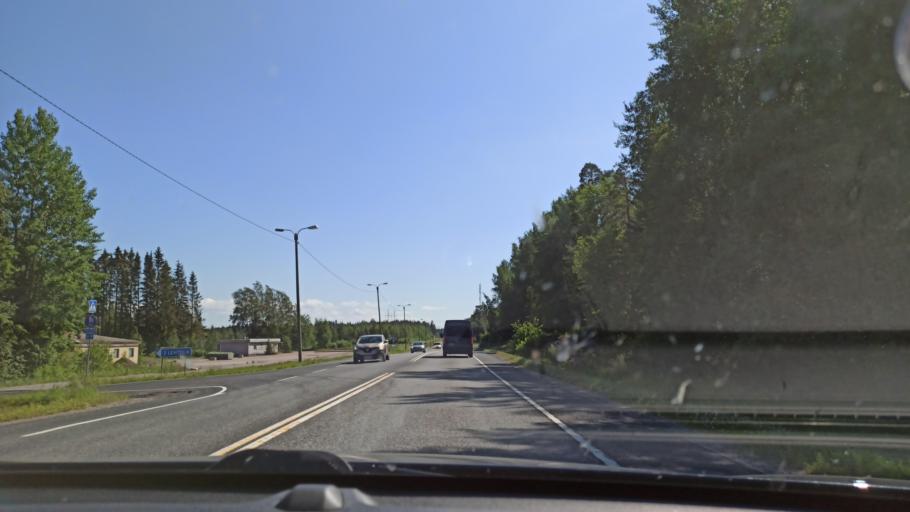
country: FI
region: Satakunta
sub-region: Pori
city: Pori
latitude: 61.5473
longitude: 21.8098
